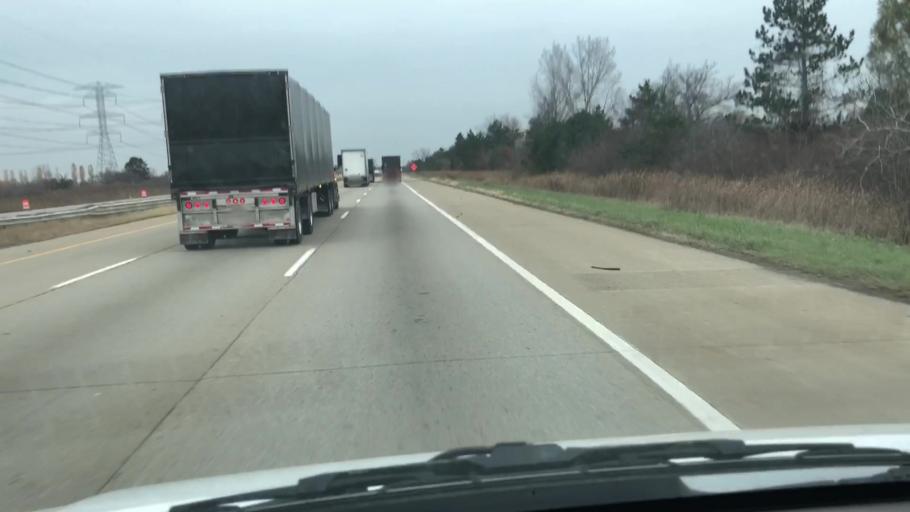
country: US
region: Michigan
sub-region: Monroe County
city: South Rockwood
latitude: 42.0441
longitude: -83.2800
